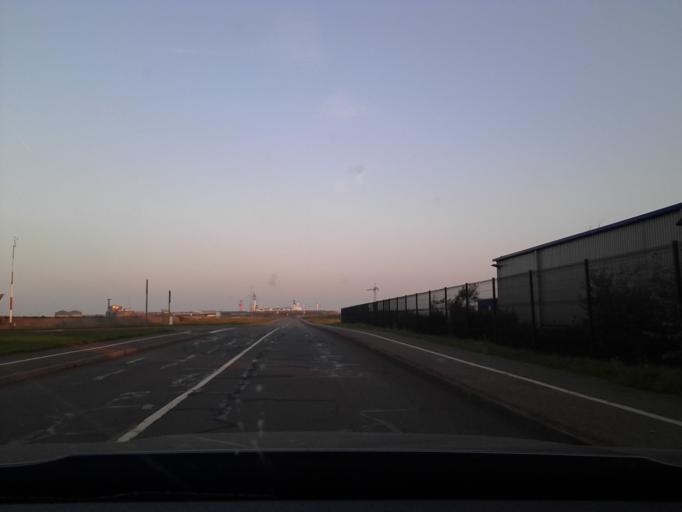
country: FR
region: Nord-Pas-de-Calais
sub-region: Departement du Nord
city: Saint-Pol-sur-Mer
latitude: 51.0532
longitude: 2.3423
